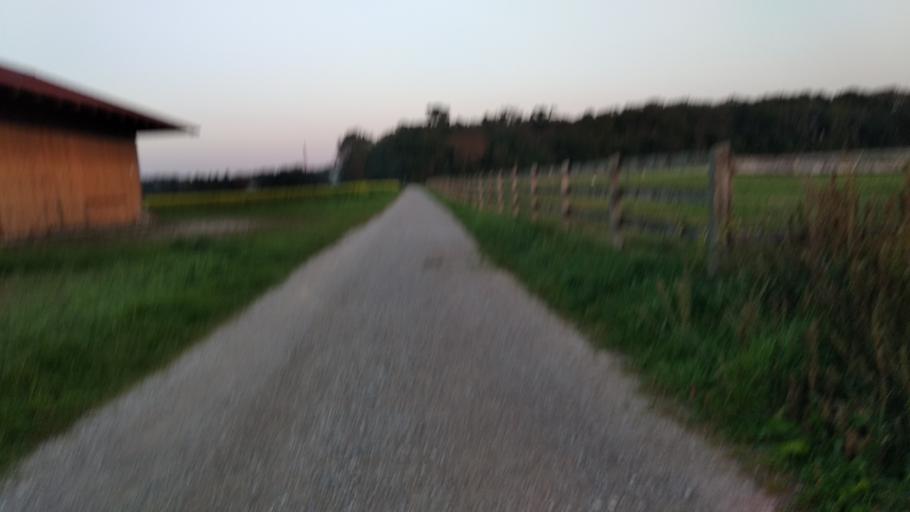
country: DE
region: Bavaria
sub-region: Upper Bavaria
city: Hohenbrunn
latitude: 48.0444
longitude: 11.7136
